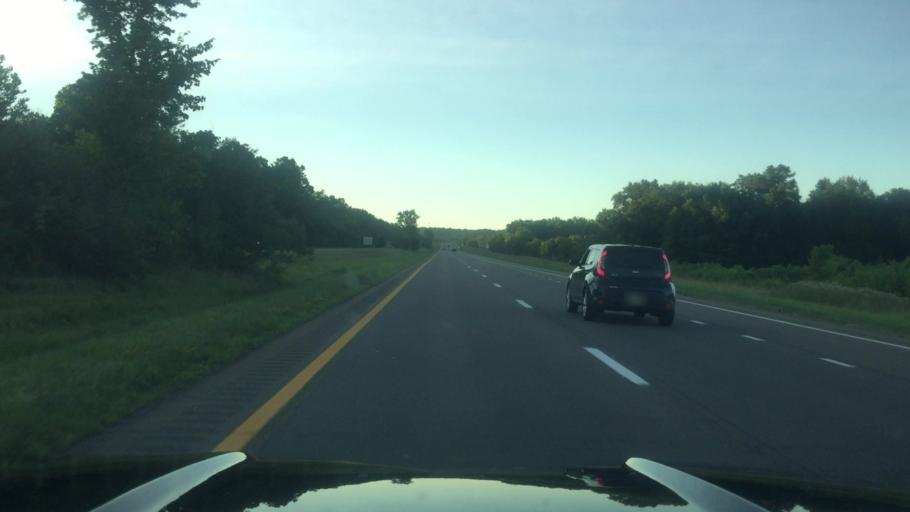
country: US
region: Ohio
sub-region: Tuscarawas County
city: Strasburg
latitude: 40.5549
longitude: -81.5045
